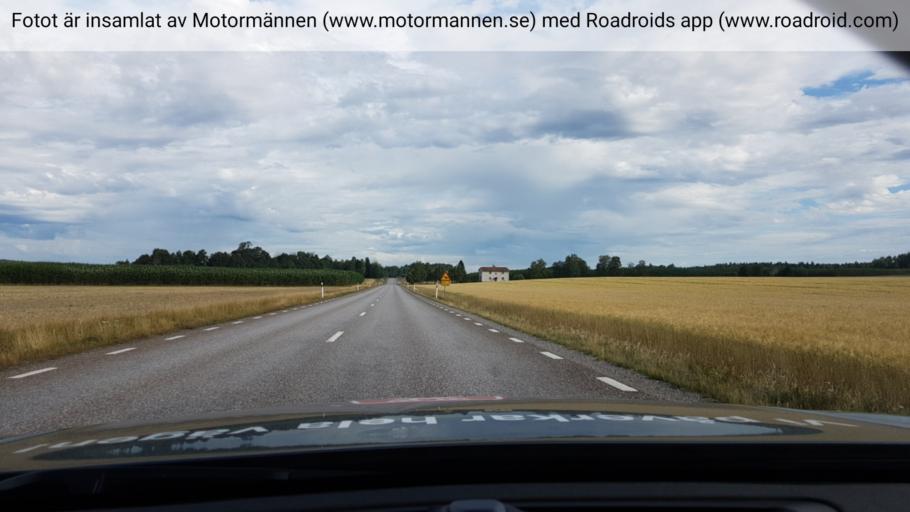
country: SE
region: Uppsala
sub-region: Heby Kommun
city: Morgongava
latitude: 59.8313
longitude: 16.9270
